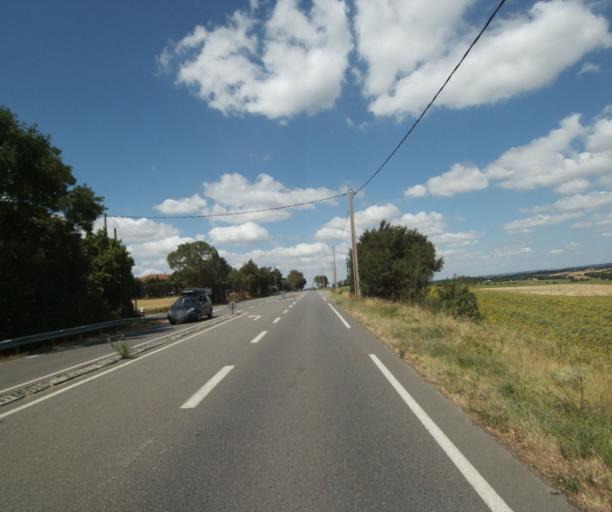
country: FR
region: Midi-Pyrenees
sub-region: Departement de la Haute-Garonne
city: Saint-Felix-Lauragais
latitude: 43.4613
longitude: 1.8358
